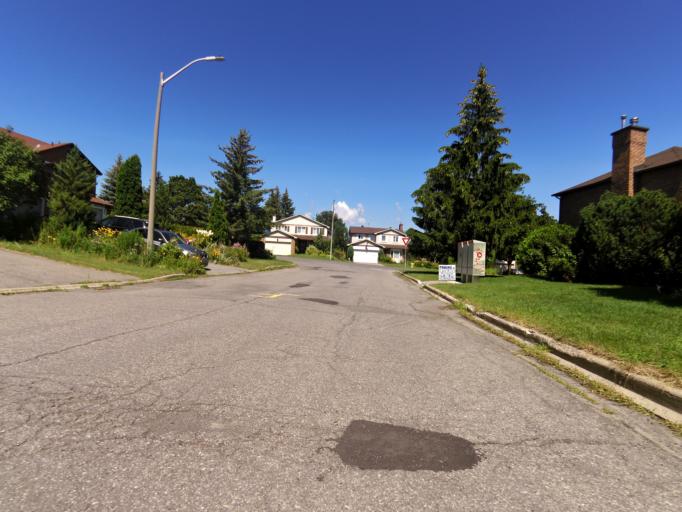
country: CA
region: Ontario
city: Ottawa
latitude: 45.3494
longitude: -75.6611
